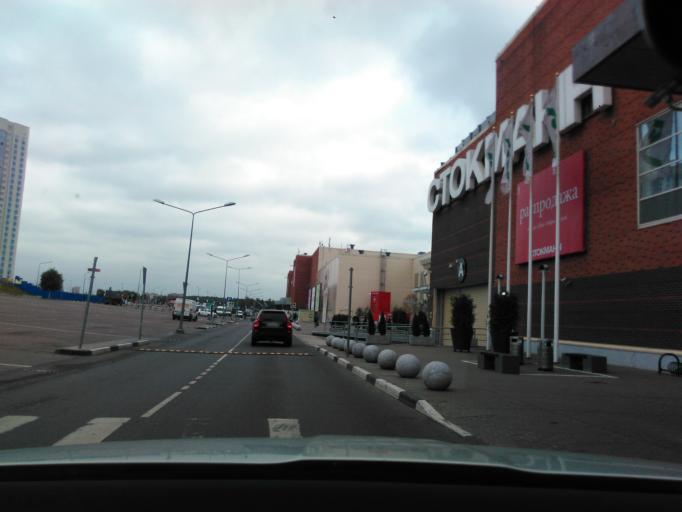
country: RU
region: Moscow
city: Khimki
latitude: 55.9088
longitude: 37.3966
